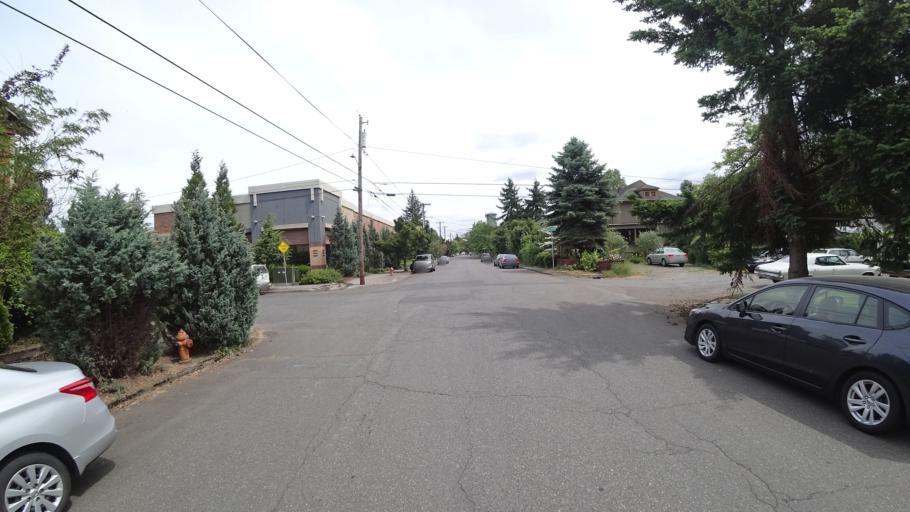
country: US
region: Oregon
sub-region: Washington County
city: West Haven
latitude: 45.5878
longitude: -122.7544
